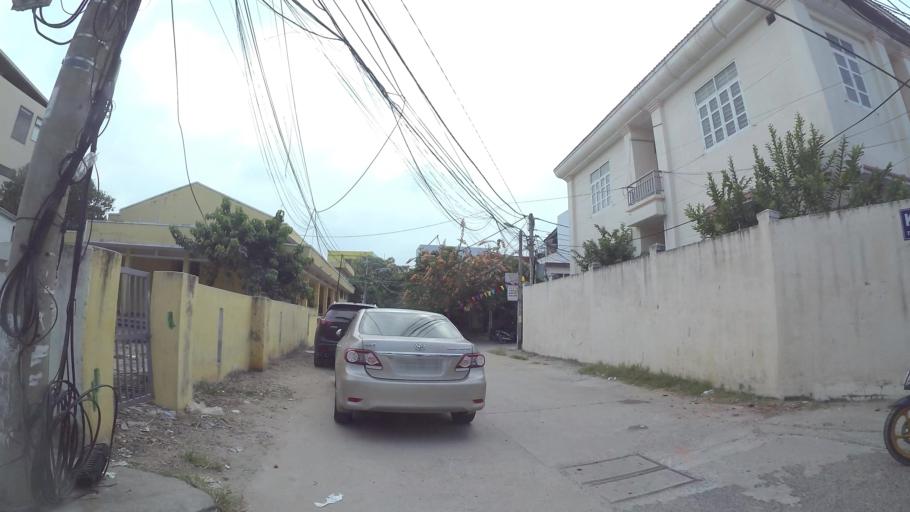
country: VN
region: Da Nang
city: Son Tra
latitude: 16.0613
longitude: 108.2424
